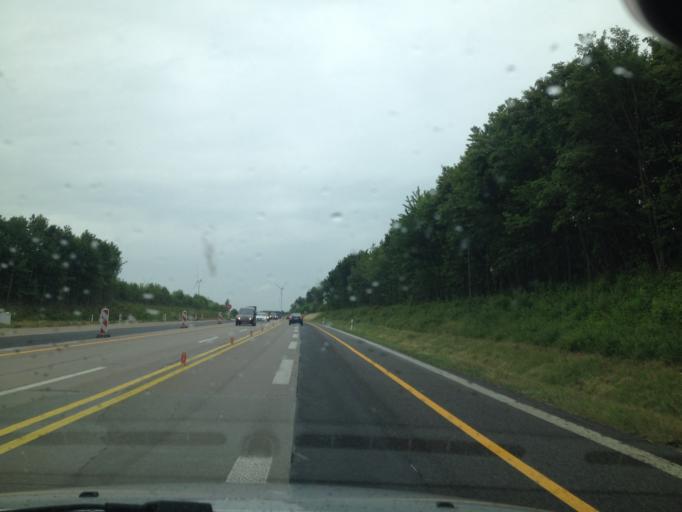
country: DE
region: Bavaria
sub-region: Regierungsbezirk Mittelfranken
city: Uffenheim
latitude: 49.5115
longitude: 10.1974
